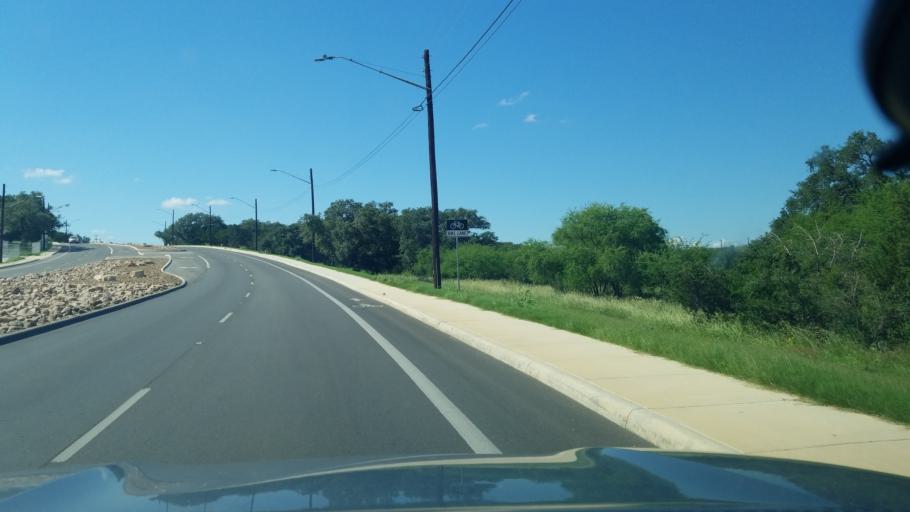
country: US
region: Texas
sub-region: Bexar County
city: Hollywood Park
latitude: 29.5974
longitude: -98.4373
